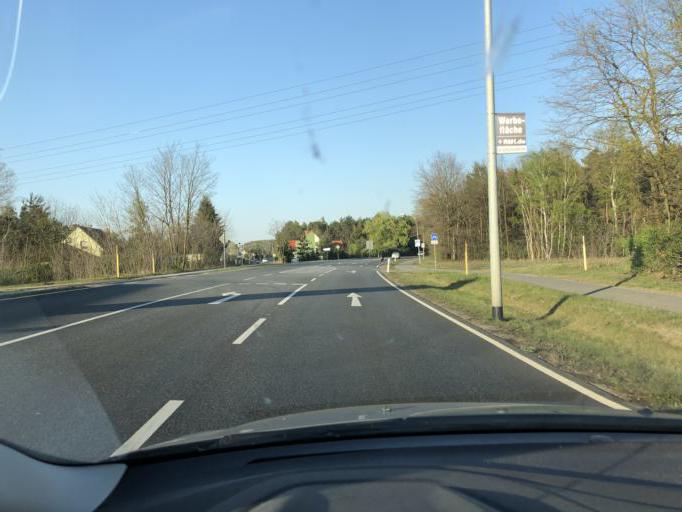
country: DE
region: Brandenburg
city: Ruhland
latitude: 51.4757
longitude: 13.8996
